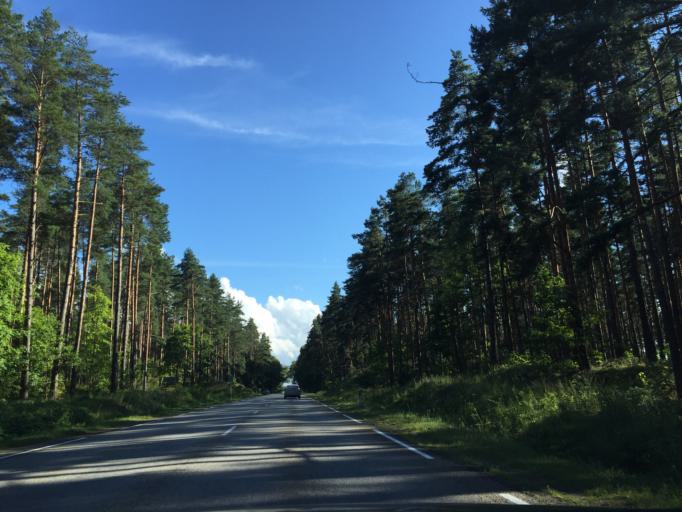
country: LV
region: Riga
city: Jaunciems
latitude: 57.0574
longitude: 24.1559
